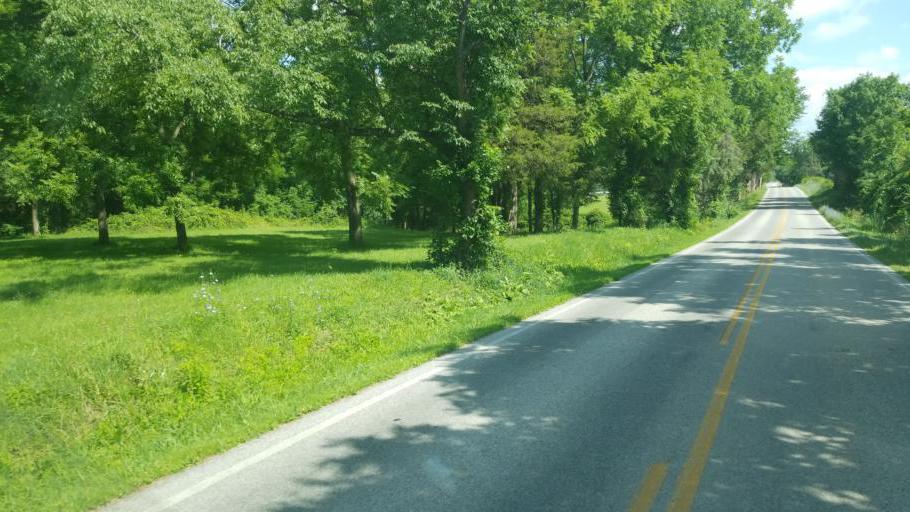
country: US
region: Ohio
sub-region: Delaware County
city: Sunbury
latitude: 40.2706
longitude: -82.9386
